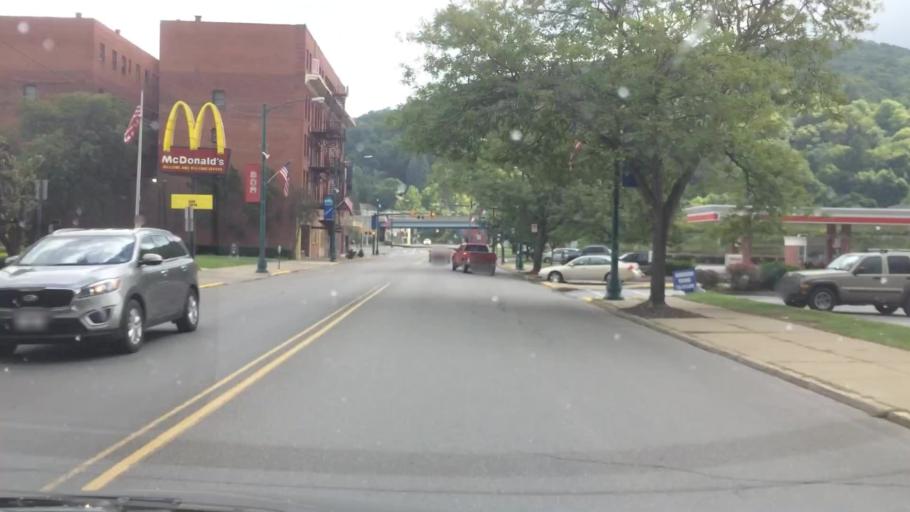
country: US
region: Pennsylvania
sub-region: McKean County
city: Bradford
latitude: 41.9561
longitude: -78.6473
